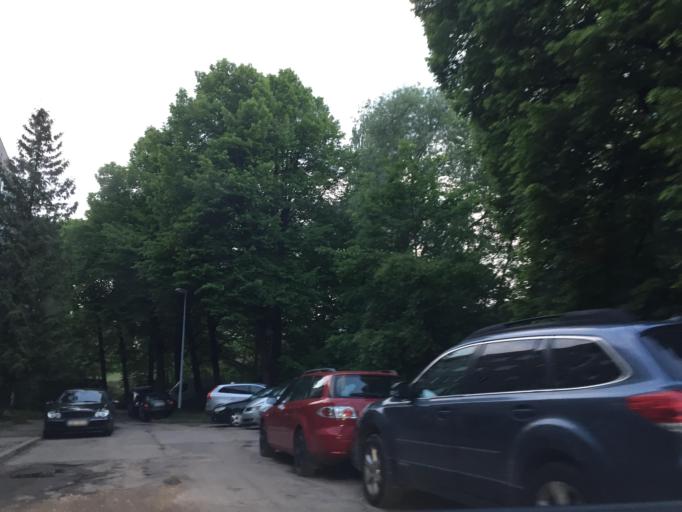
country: LV
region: Riga
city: Riga
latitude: 56.9733
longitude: 24.0604
